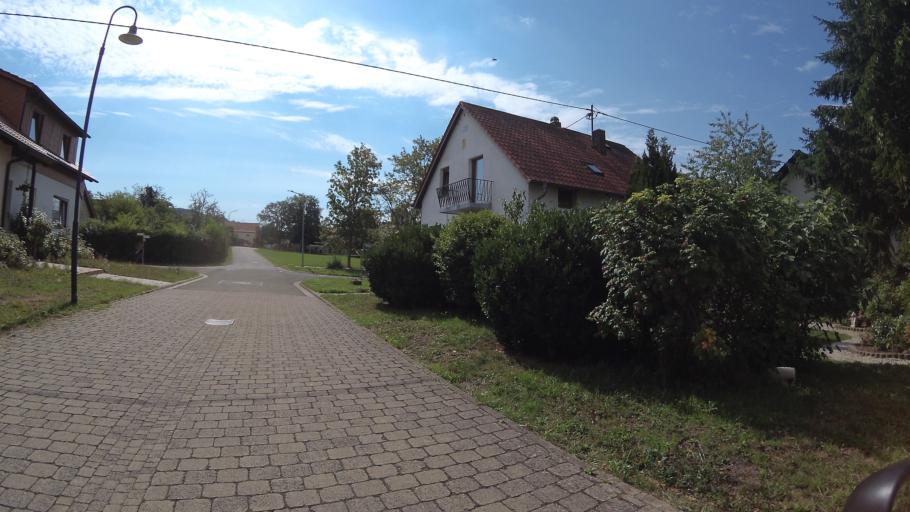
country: DE
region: Saarland
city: Gersheim
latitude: 49.1351
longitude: 7.2054
